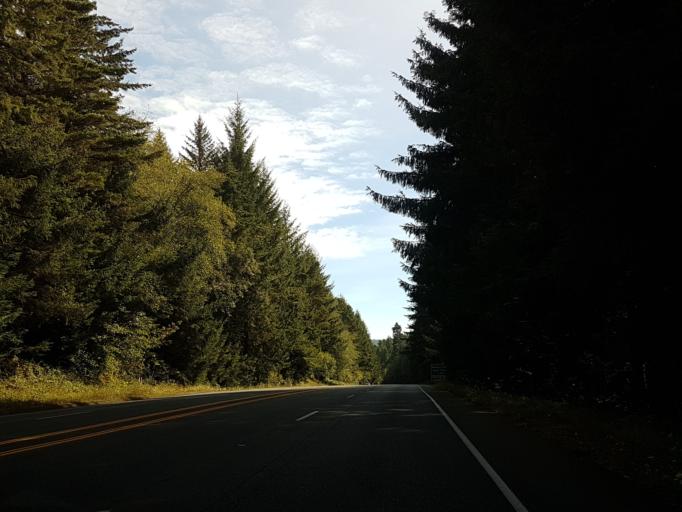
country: US
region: California
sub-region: Del Norte County
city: Bertsch-Oceanview
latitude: 41.4812
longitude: -124.0494
